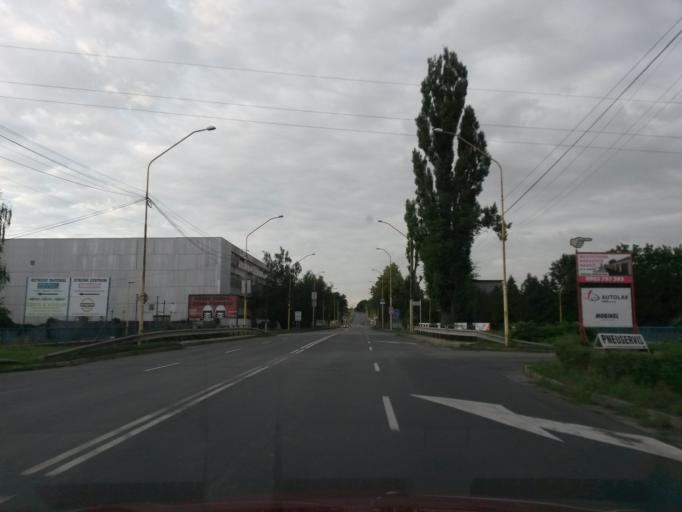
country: SK
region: Banskobystricky
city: Lucenec
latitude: 48.3363
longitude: 19.6761
